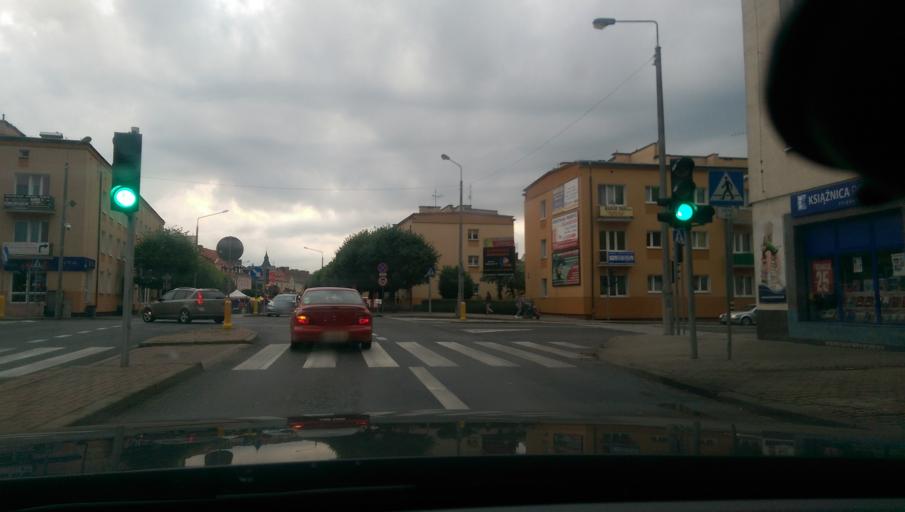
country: PL
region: Warmian-Masurian Voivodeship
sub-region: Powiat szczycienski
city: Szczytno
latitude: 53.5634
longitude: 20.9954
